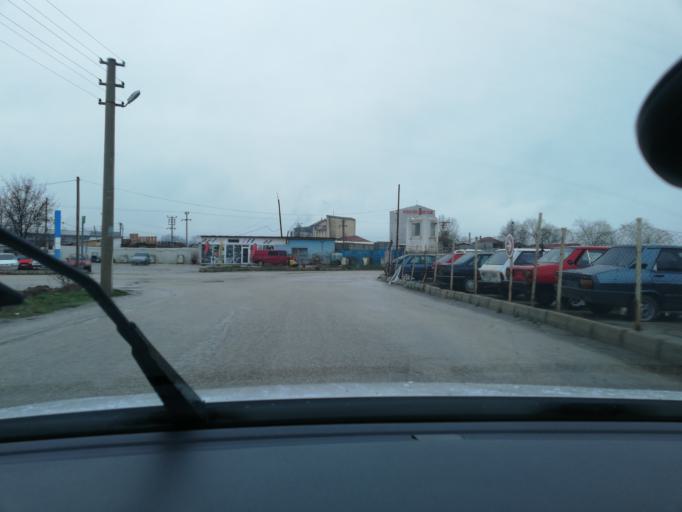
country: TR
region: Bolu
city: Bolu
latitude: 40.7378
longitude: 31.6328
